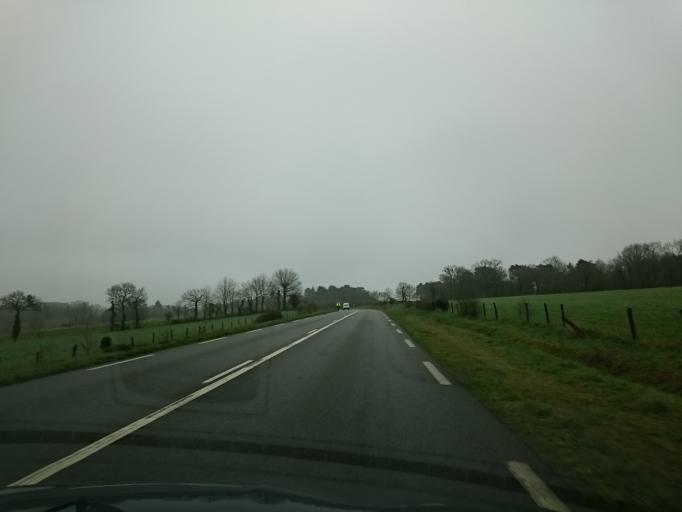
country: FR
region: Brittany
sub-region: Departement d'Ille-et-Vilaine
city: Bourg-des-Comptes
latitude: 47.9277
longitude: -1.7257
